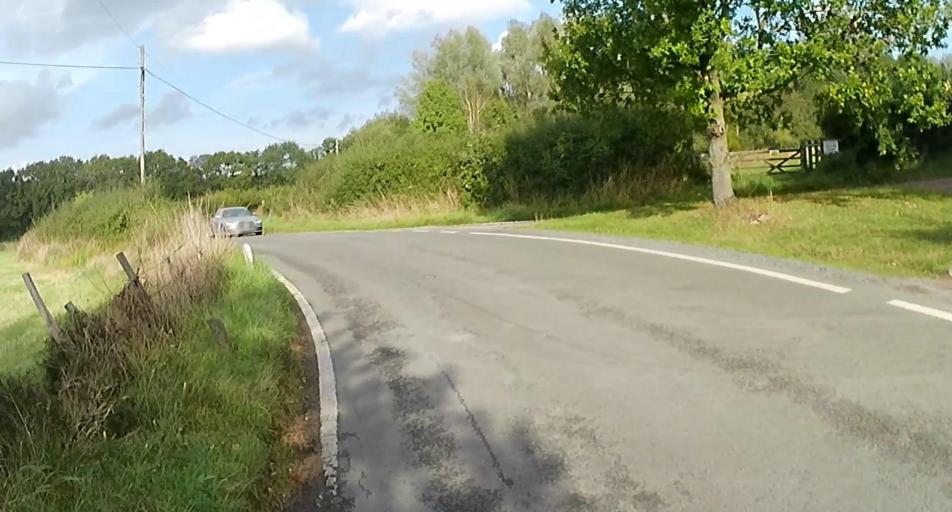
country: GB
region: England
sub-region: Hampshire
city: Tadley
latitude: 51.3325
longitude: -1.1724
